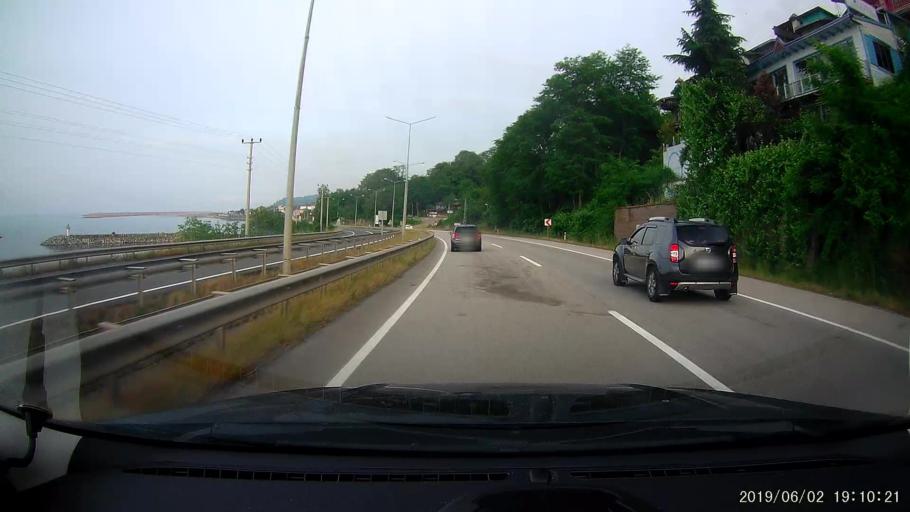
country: TR
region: Ordu
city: Gulyali
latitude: 40.9695
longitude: 38.0431
